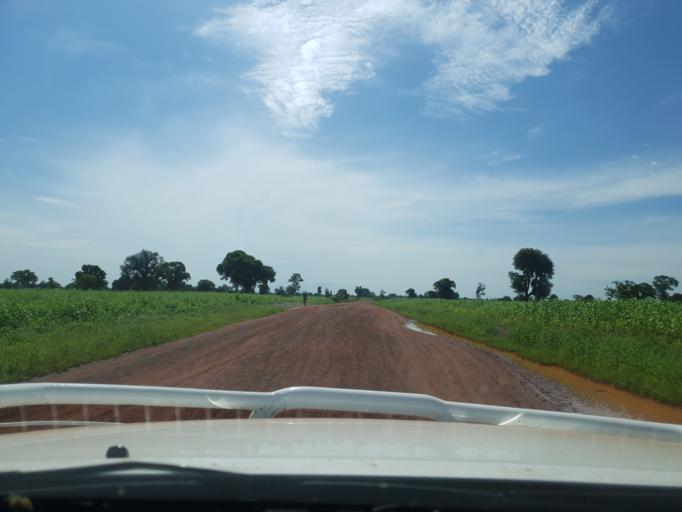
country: ML
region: Koulikoro
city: Banamba
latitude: 13.2814
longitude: -7.5547
